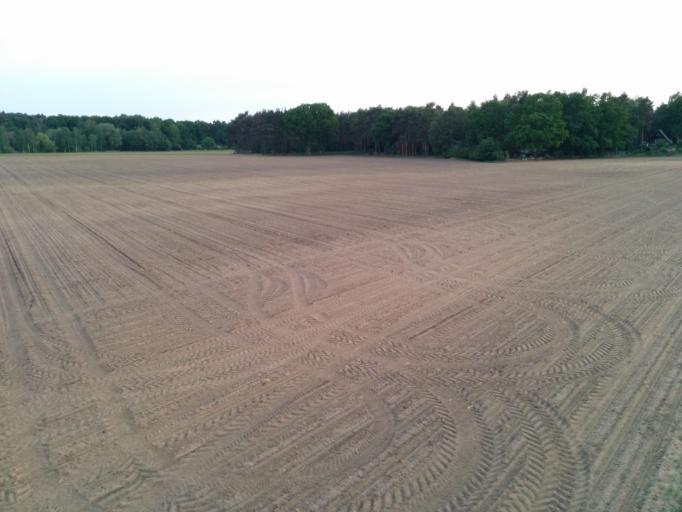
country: DE
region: Lower Saxony
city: Meinersen
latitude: 52.4490
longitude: 10.3803
